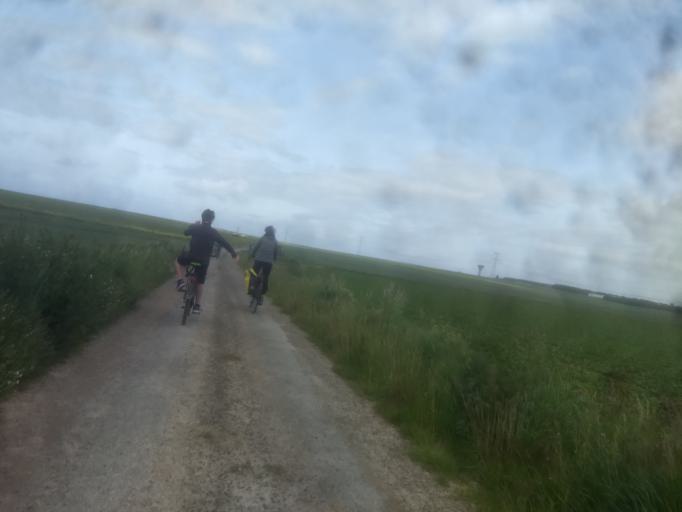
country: FR
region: Nord-Pas-de-Calais
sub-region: Departement du Pas-de-Calais
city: Feuchy
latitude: 50.2818
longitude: 2.8413
